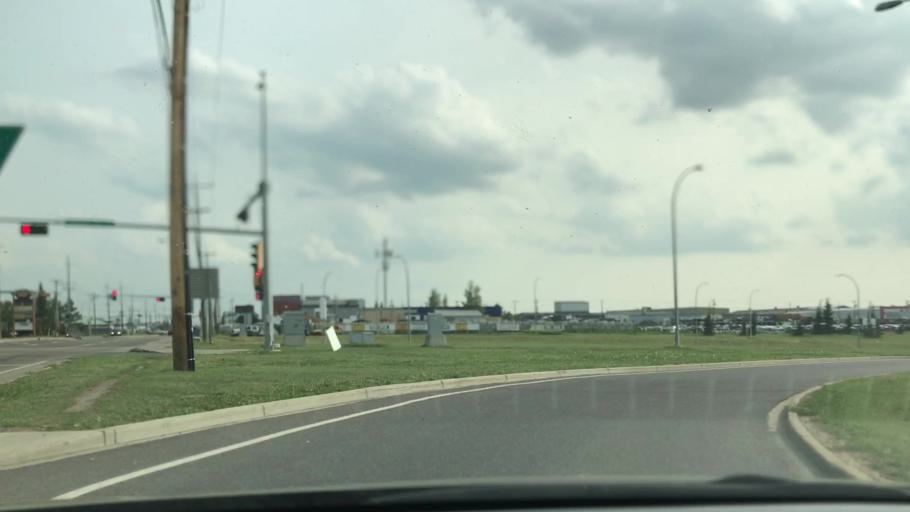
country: CA
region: Alberta
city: Edmonton
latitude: 53.5151
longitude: -113.4187
